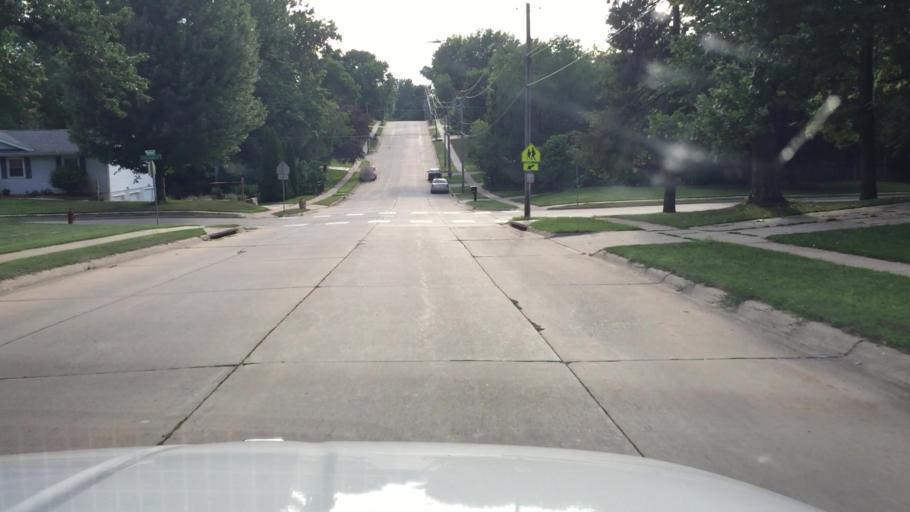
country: US
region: Iowa
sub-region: Johnson County
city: Iowa City
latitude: 41.6605
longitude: -91.4980
